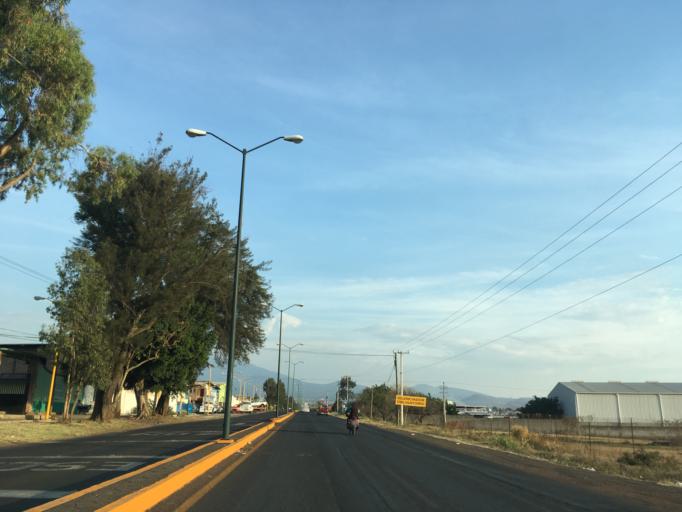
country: MX
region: Michoacan
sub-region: Los Reyes
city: La Higuerita (Colonia San Rafael)
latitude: 19.6131
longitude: -102.4826
